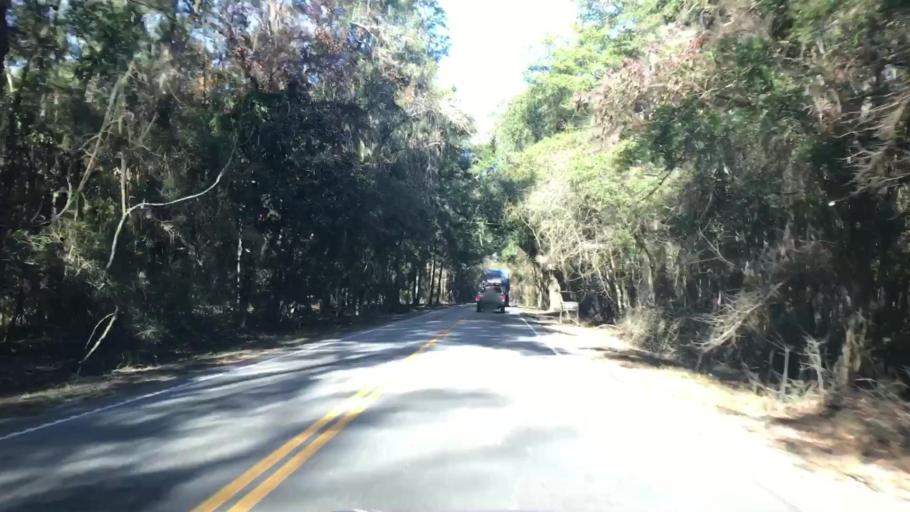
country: US
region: South Carolina
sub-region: Charleston County
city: Shell Point
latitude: 32.8658
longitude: -80.0843
